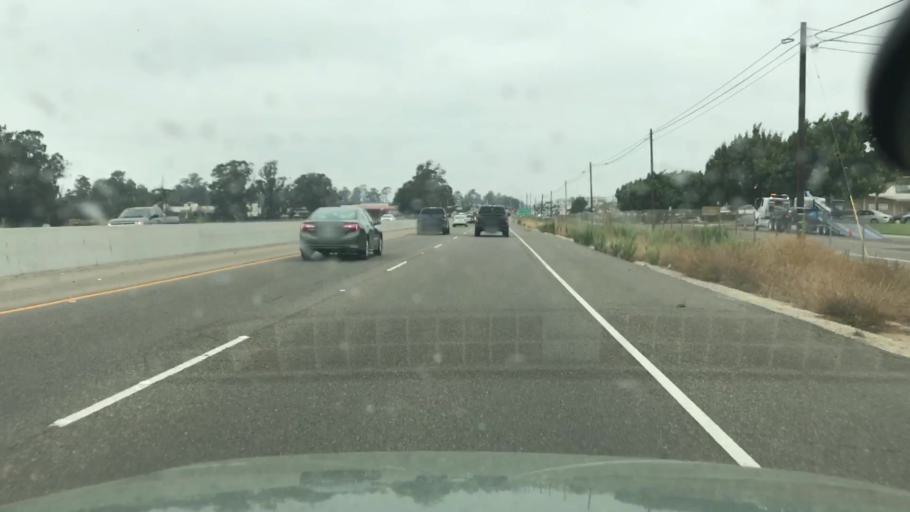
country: US
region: California
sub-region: Santa Barbara County
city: Orcutt
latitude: 34.8905
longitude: -120.4364
